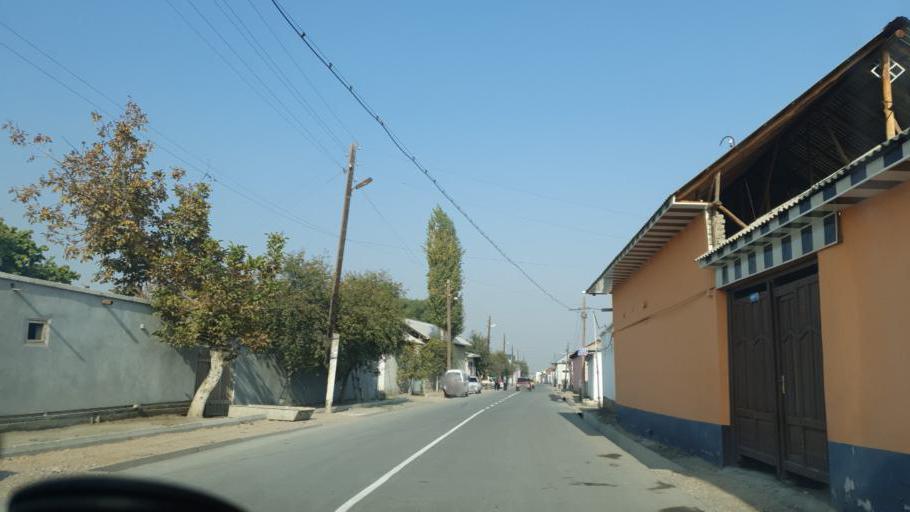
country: UZ
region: Fergana
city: Qo`qon
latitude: 40.5837
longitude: 70.9087
